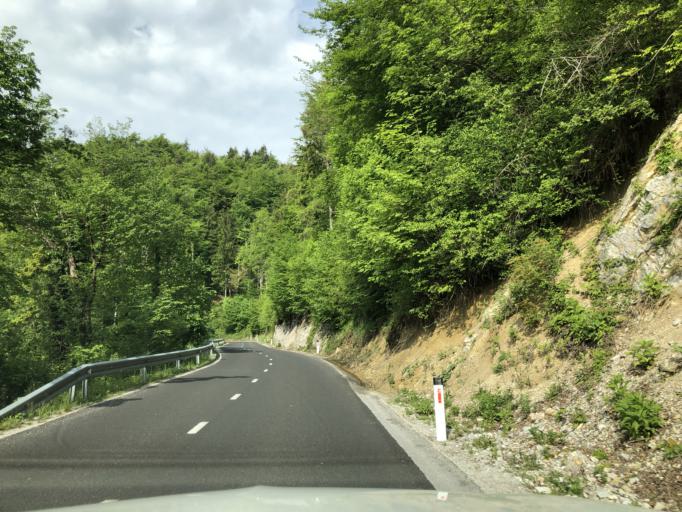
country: SI
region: Bloke
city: Nova Vas
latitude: 45.8000
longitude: 14.5619
